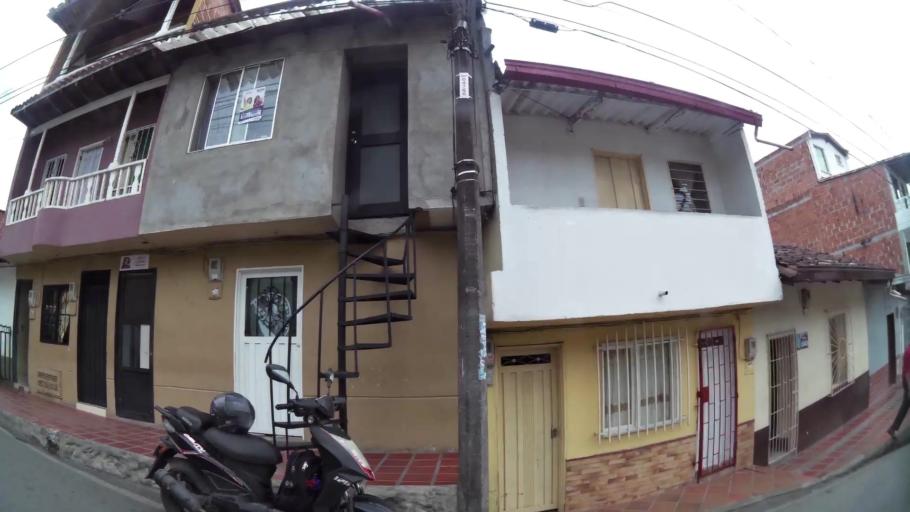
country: CO
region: Antioquia
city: Rionegro
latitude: 6.1549
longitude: -75.3657
